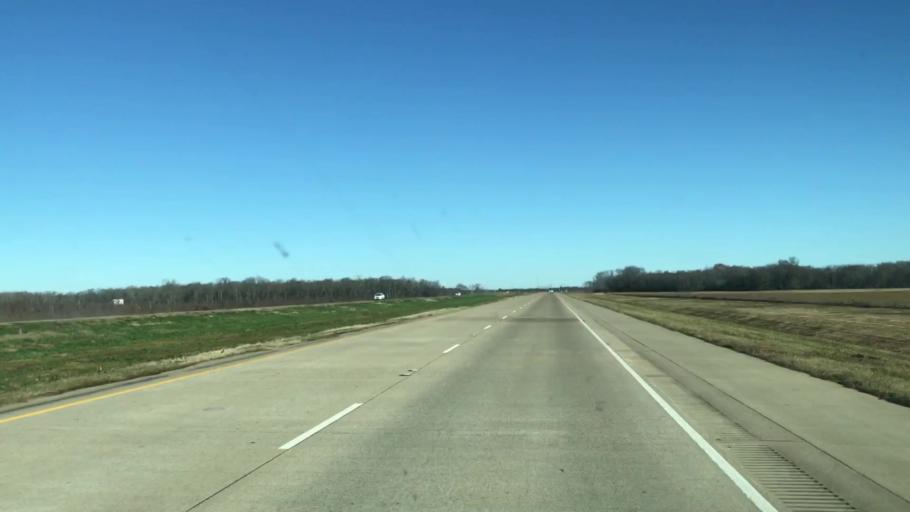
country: US
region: Louisiana
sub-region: Caddo Parish
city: Blanchard
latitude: 32.6365
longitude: -93.8381
